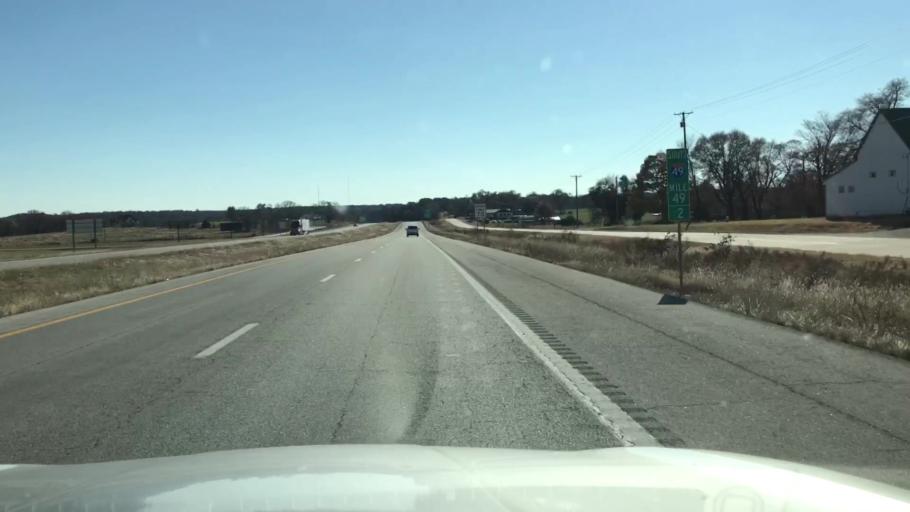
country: US
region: Missouri
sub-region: Jasper County
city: Carthage
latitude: 37.1217
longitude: -94.3112
